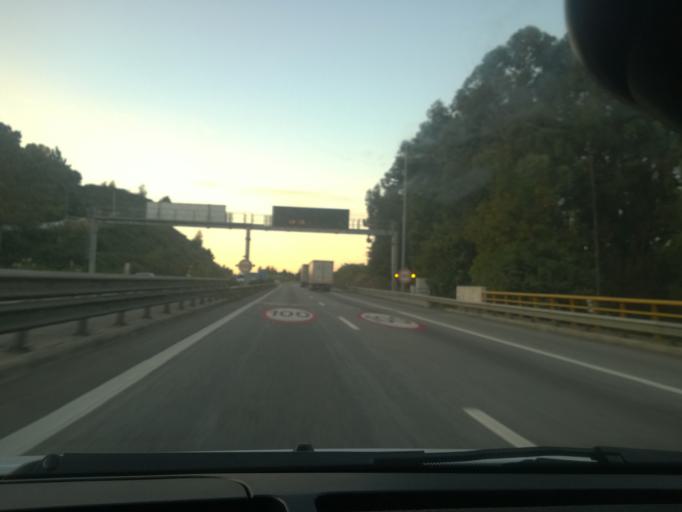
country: PT
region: Porto
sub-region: Vila Nova de Gaia
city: Oliveira do Douro
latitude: 41.1249
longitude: -8.5737
